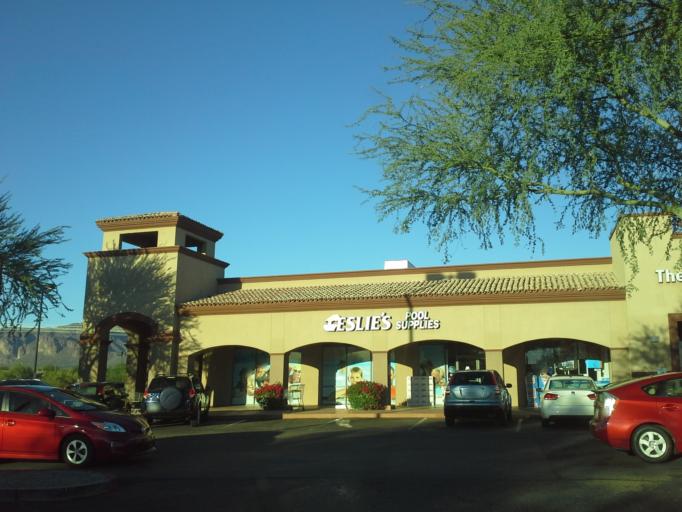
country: US
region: Arizona
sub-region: Pinal County
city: Apache Junction
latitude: 33.3667
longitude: -111.4756
